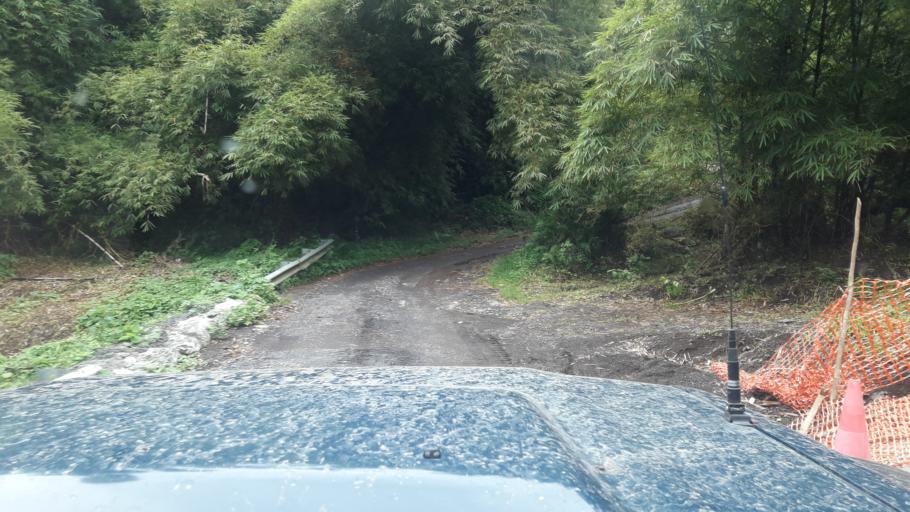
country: VU
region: Shefa
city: Port-Vila
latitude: -16.9102
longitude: 168.5298
